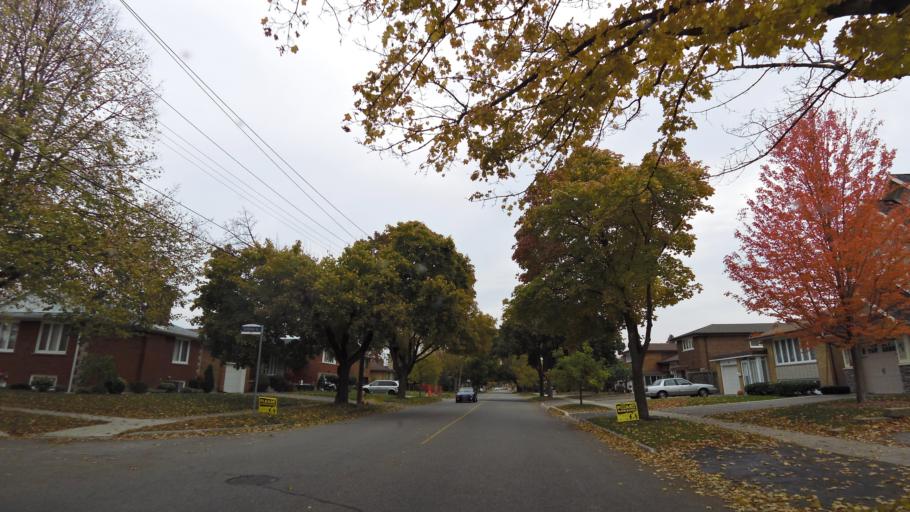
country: CA
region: Ontario
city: Etobicoke
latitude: 43.6849
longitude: -79.5324
